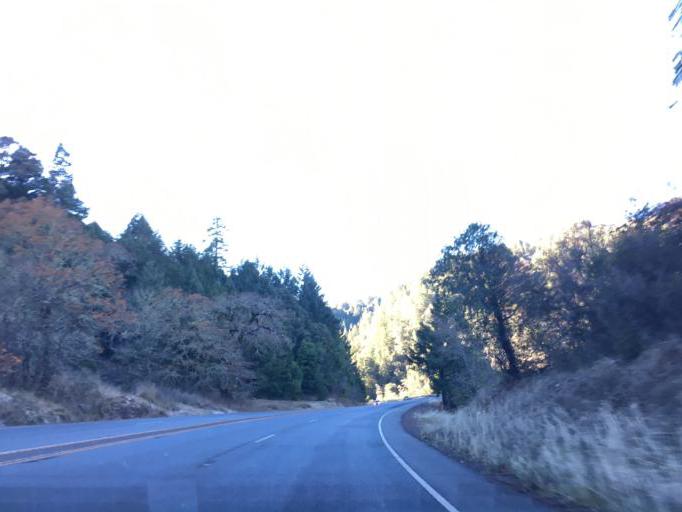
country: US
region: California
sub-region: Mendocino County
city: Laytonville
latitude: 39.8267
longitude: -123.5838
